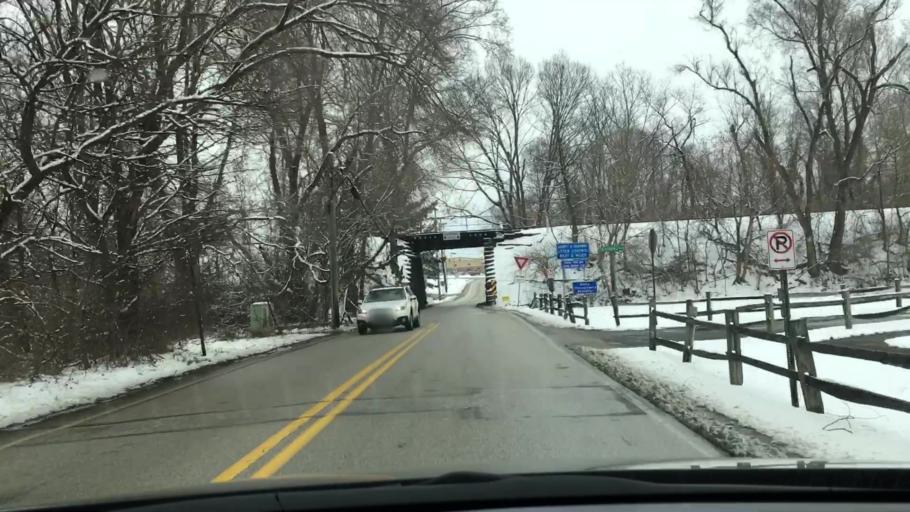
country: US
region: Pennsylvania
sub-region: York County
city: Emigsville
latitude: 40.0183
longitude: -76.7270
